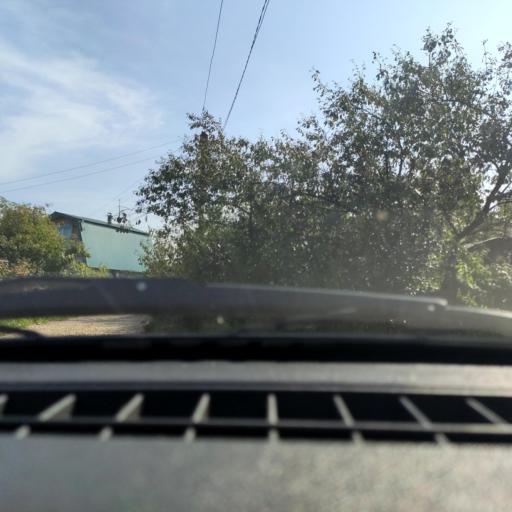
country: RU
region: Bashkortostan
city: Blagoveshchensk
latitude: 54.9411
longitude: 56.0907
